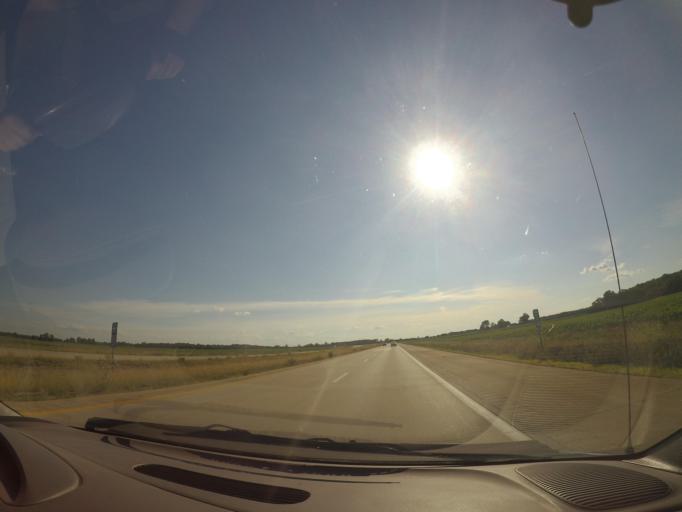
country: US
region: Ohio
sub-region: Lucas County
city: Whitehouse
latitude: 41.4339
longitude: -83.8751
